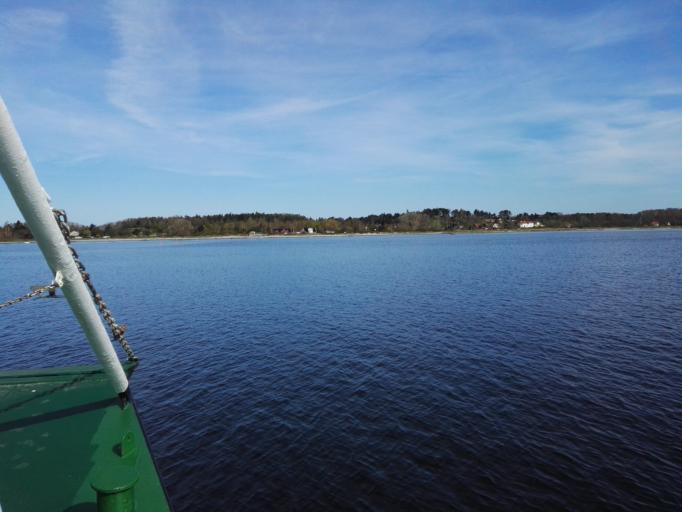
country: DK
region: Capital Region
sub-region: Halsnaes Kommune
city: Hundested
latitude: 55.9412
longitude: 11.9050
